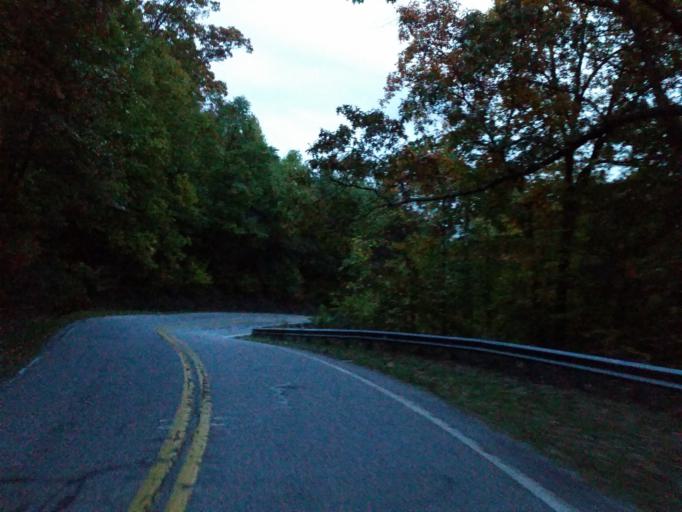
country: US
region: Georgia
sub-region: Lumpkin County
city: Dahlonega
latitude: 34.6501
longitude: -83.9689
